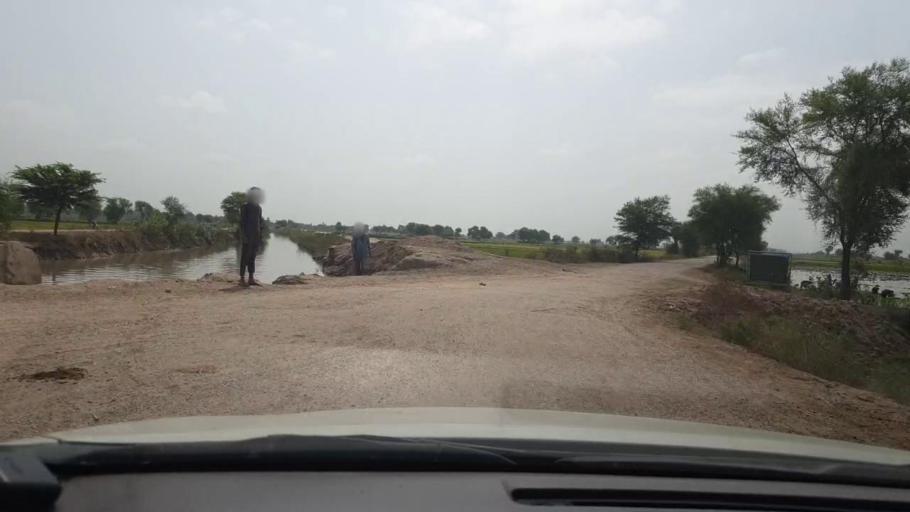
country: PK
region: Sindh
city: Shikarpur
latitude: 28.0064
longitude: 68.5809
